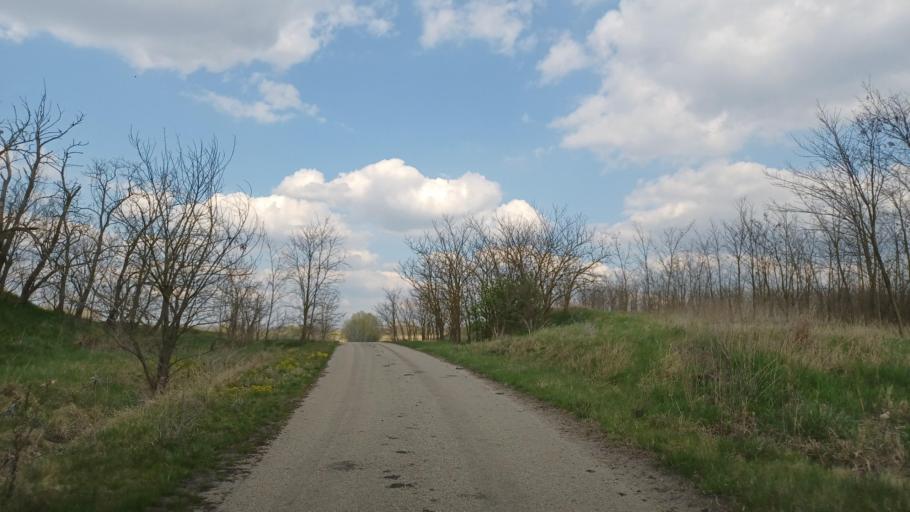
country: HU
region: Fejer
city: Cece
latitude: 46.7392
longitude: 18.6366
